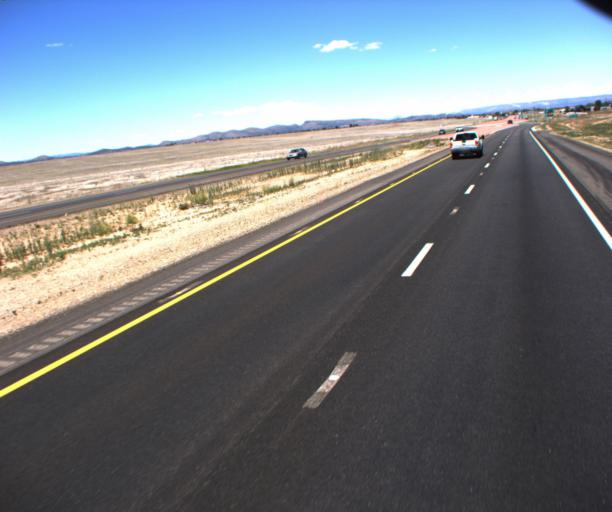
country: US
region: Arizona
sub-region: Yavapai County
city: Chino Valley
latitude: 34.7015
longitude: -112.4493
